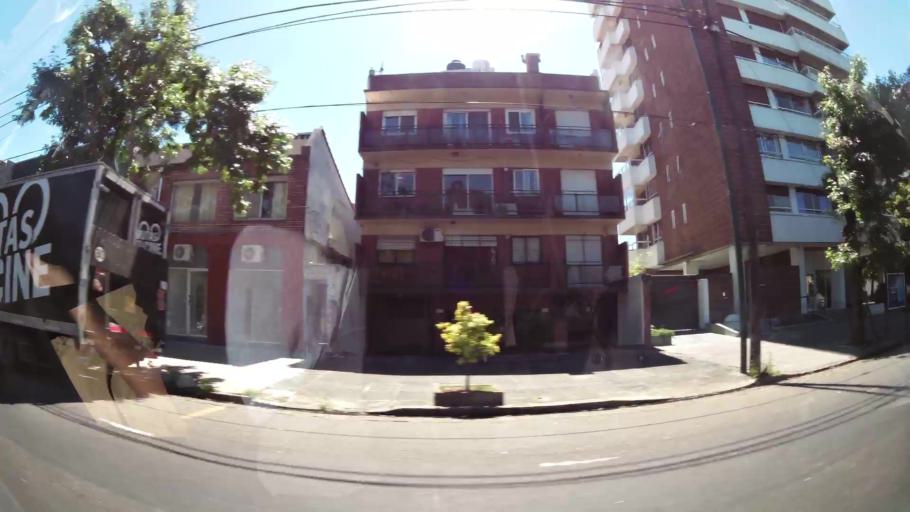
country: AR
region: Buenos Aires
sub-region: Partido de San Isidro
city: San Isidro
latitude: -34.4784
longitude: -58.5086
